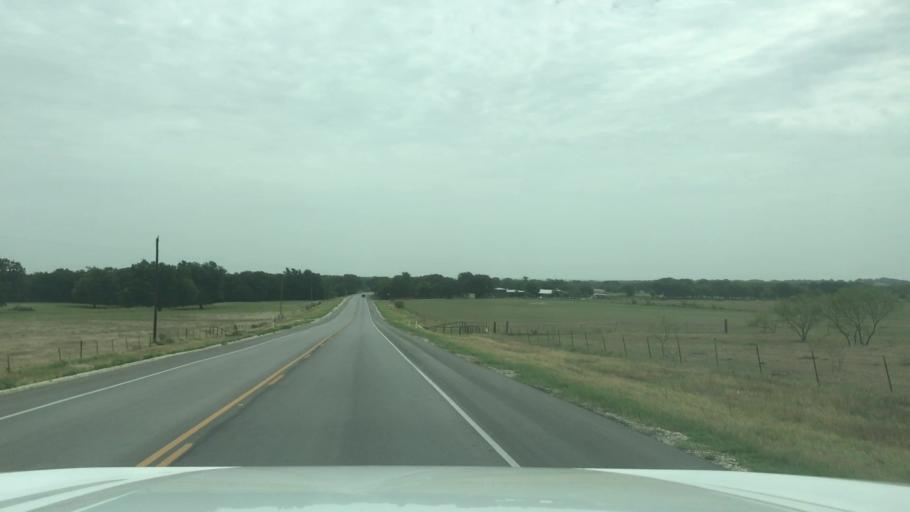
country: US
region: Texas
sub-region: Erath County
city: Dublin
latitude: 32.0869
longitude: -98.3097
